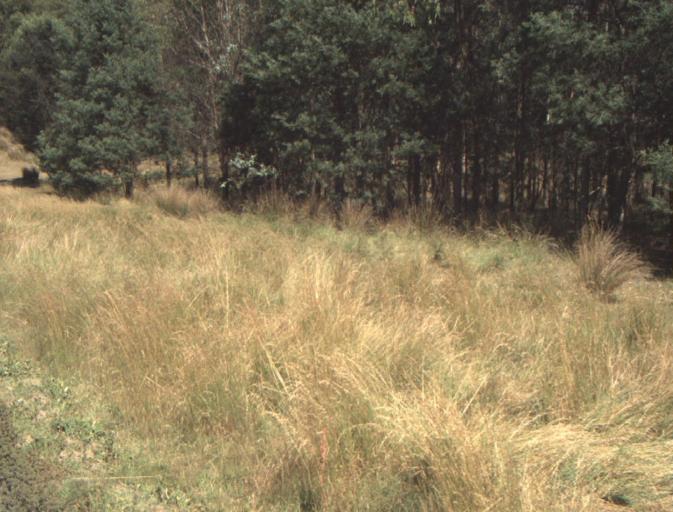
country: AU
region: Tasmania
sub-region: Dorset
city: Scottsdale
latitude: -41.2702
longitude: 147.3517
